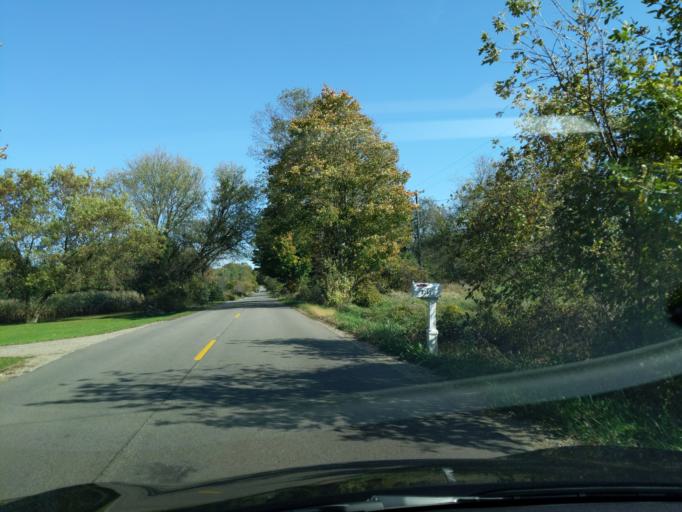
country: US
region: Michigan
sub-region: Eaton County
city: Potterville
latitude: 42.6404
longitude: -84.7742
